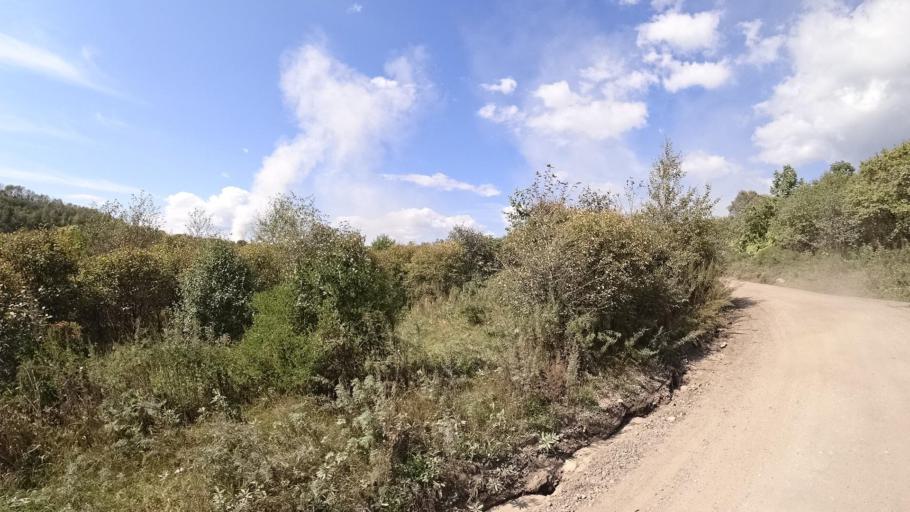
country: RU
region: Jewish Autonomous Oblast
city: Londoko
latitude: 49.0076
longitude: 131.9138
